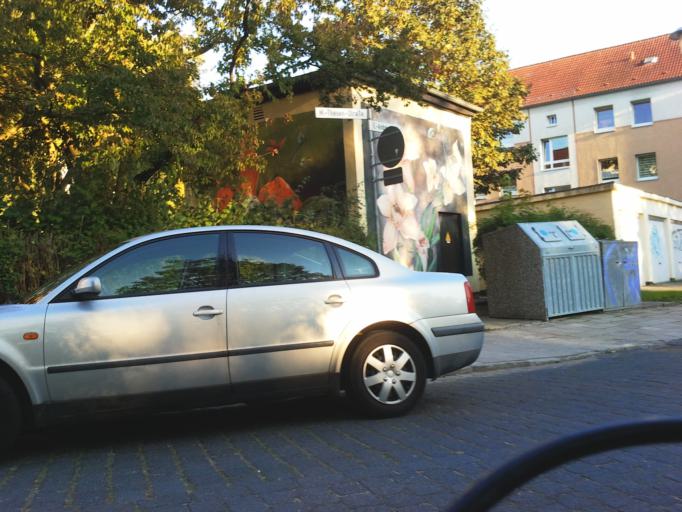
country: DE
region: Mecklenburg-Vorpommern
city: Lambrechtshagen
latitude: 54.1009
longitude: 12.0661
